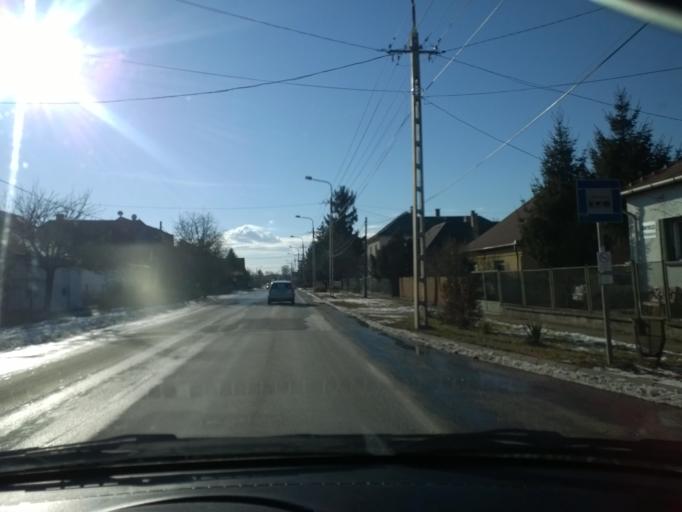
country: HU
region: Fejer
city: Martonvasar
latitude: 47.3211
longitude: 18.7958
